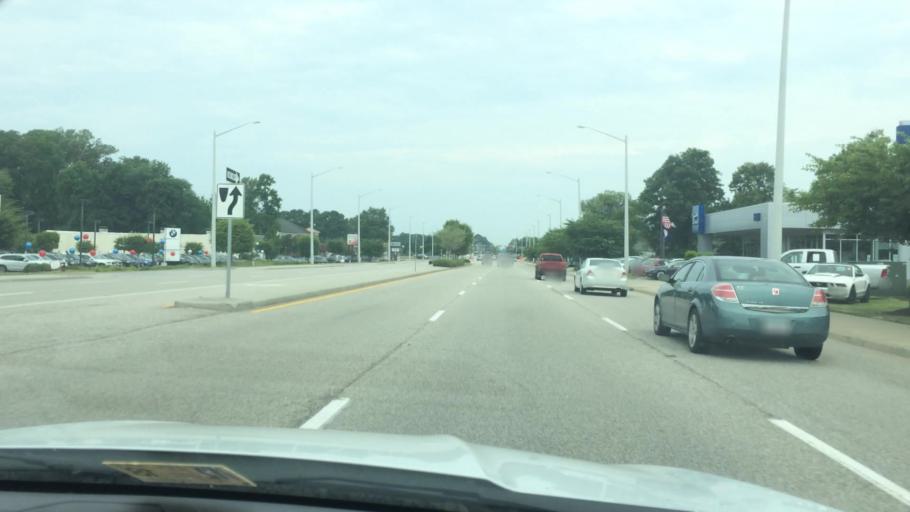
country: US
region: Virginia
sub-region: York County
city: Yorktown
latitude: 37.1450
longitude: -76.5249
